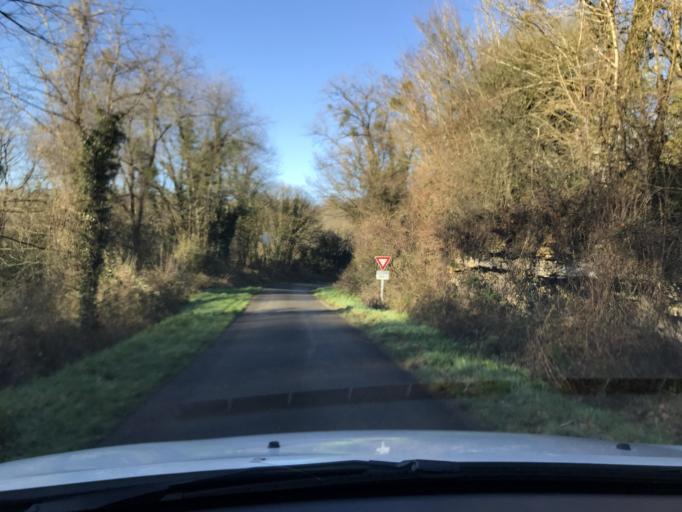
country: FR
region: Poitou-Charentes
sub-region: Departement de la Charente
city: Chasseneuil-sur-Bonnieure
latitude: 45.8434
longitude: 0.5126
